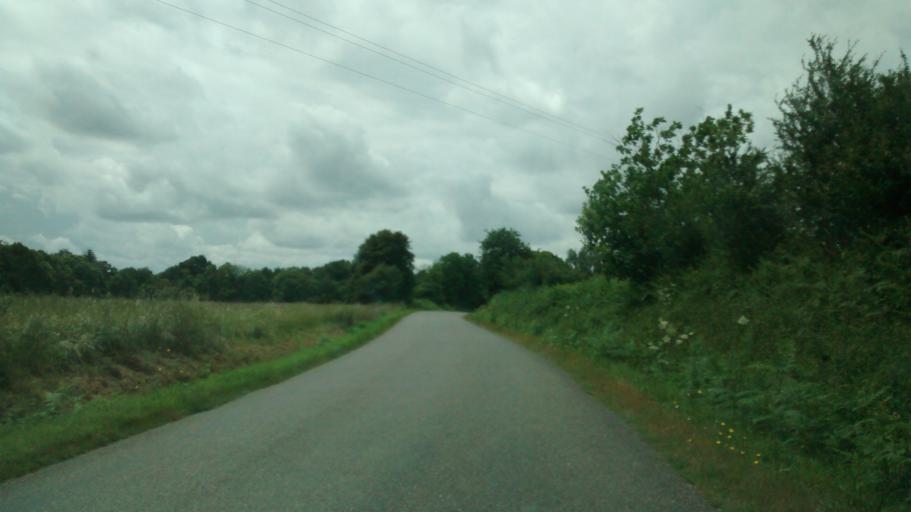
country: FR
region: Brittany
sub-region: Departement du Morbihan
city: Carentoir
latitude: 47.8195
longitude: -2.1478
